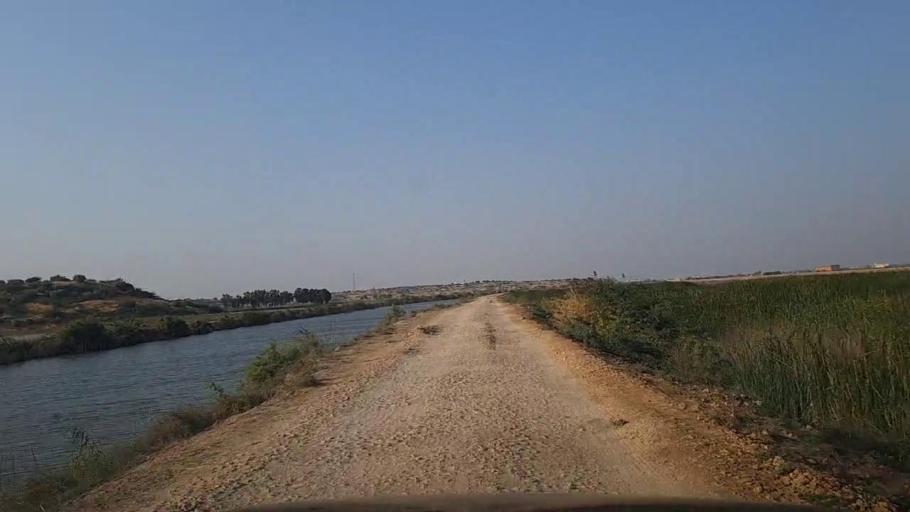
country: PK
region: Sindh
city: Thatta
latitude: 24.7335
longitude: 67.9069
